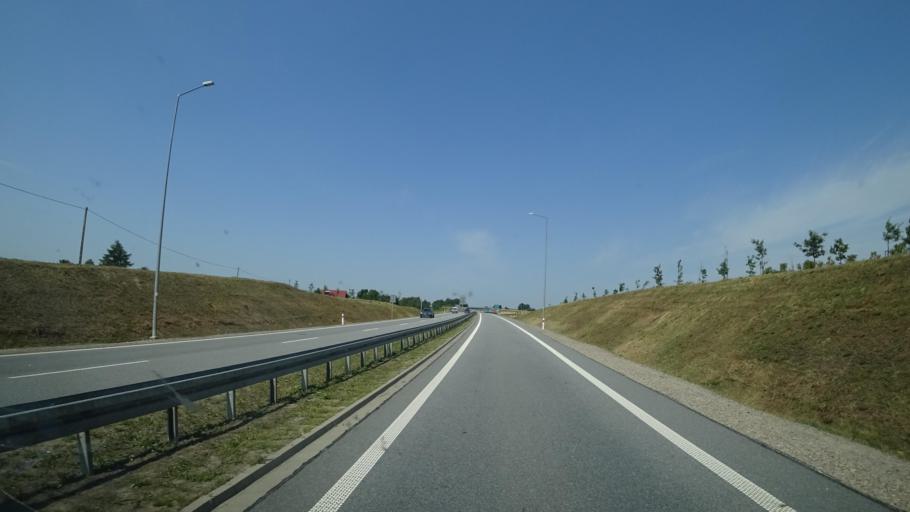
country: PL
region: Pomeranian Voivodeship
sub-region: Powiat koscierski
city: Koscierzyna
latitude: 54.1273
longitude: 18.0184
